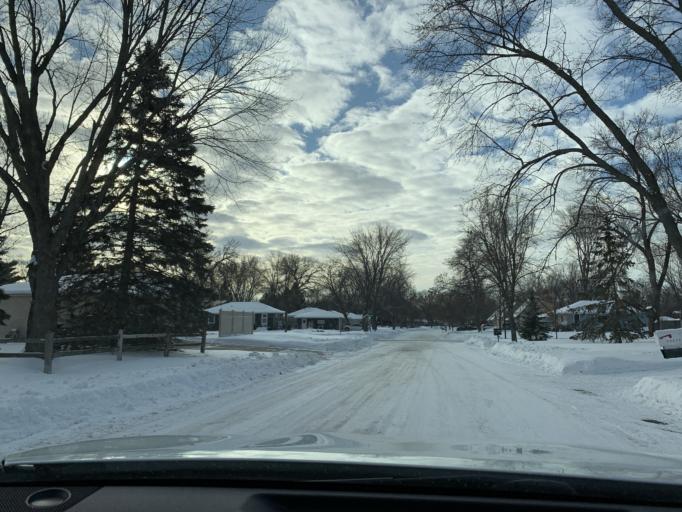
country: US
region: Minnesota
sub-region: Anoka County
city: Blaine
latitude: 45.1756
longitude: -93.2856
